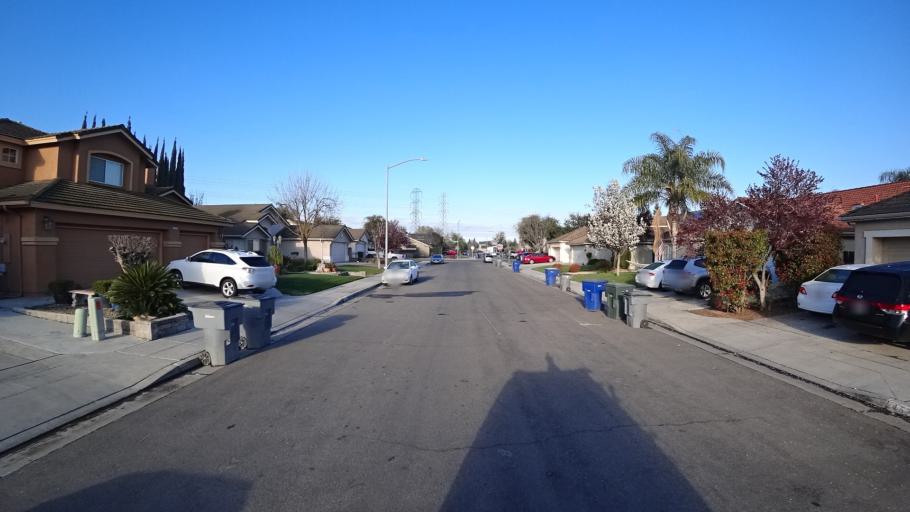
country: US
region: California
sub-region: Fresno County
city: West Park
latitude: 36.8194
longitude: -119.8757
